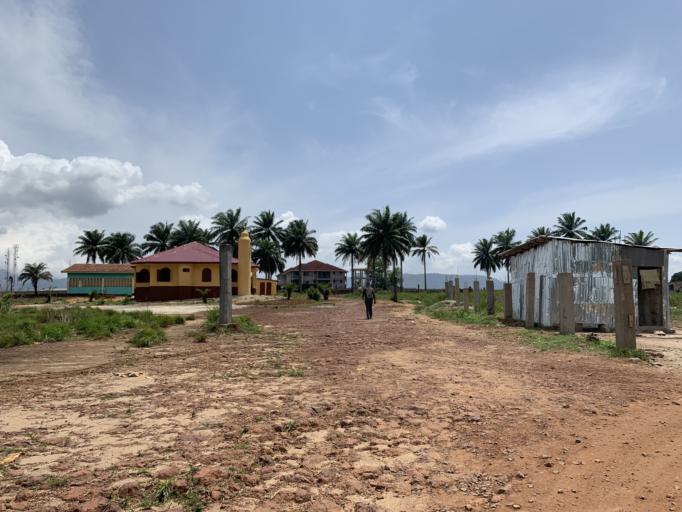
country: SL
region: Western Area
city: Waterloo
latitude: 8.3387
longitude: -13.0358
